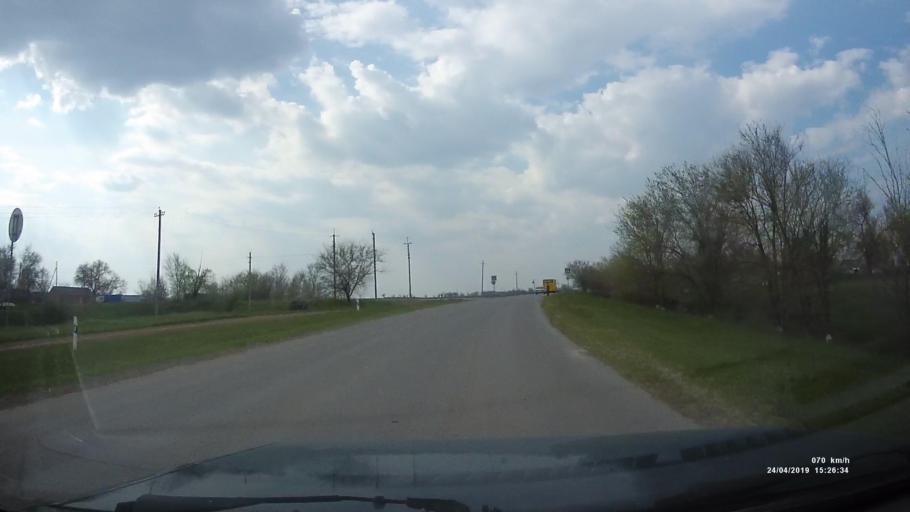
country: RU
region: Rostov
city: Remontnoye
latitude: 46.5587
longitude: 43.0312
